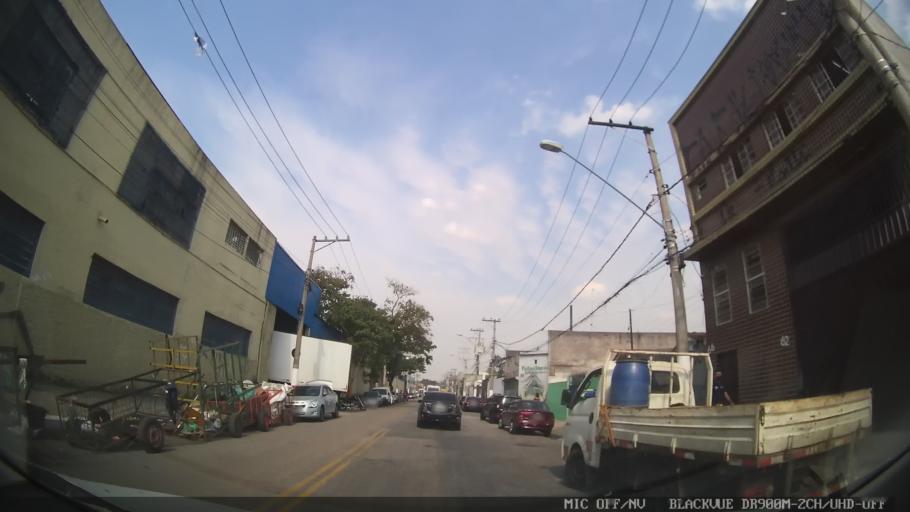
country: BR
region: Sao Paulo
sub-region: Sao Caetano Do Sul
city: Sao Caetano do Sul
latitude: -23.5991
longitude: -46.5960
